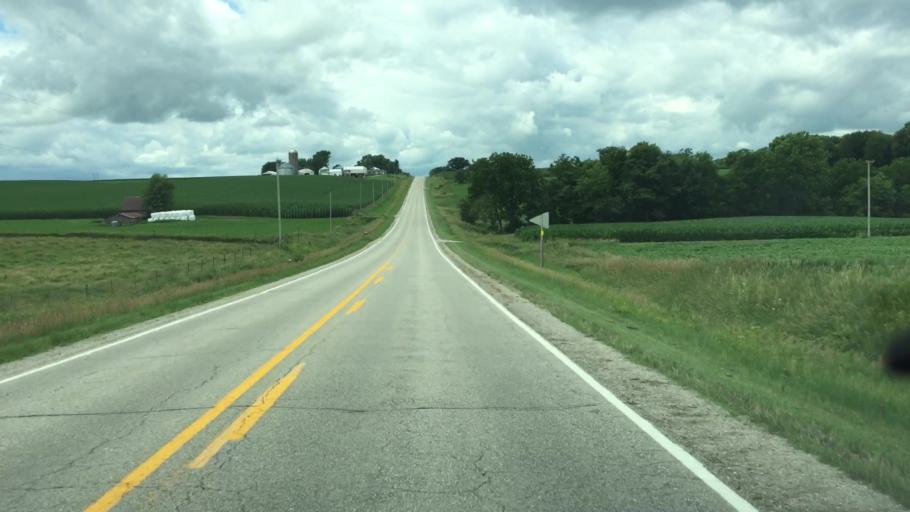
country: US
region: Iowa
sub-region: Jasper County
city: Monroe
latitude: 41.5734
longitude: -93.0529
